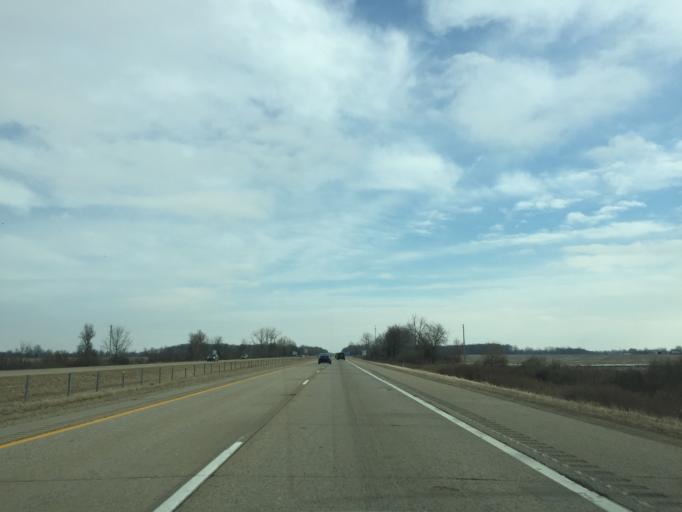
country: US
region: Michigan
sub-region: Ionia County
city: Lake Odessa
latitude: 42.8791
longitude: -85.1172
